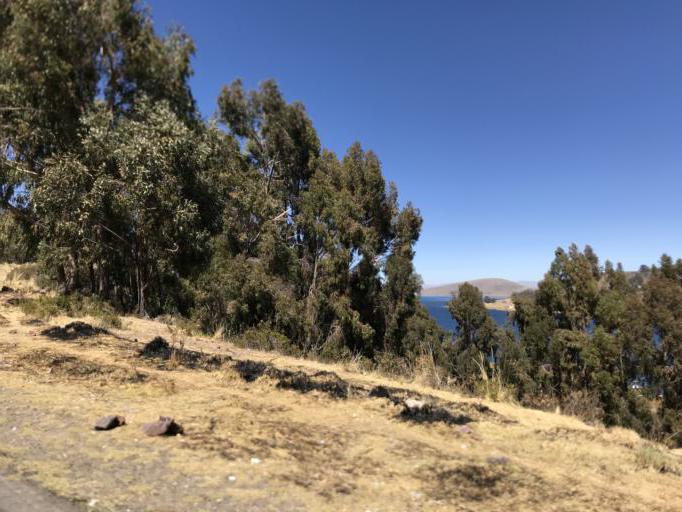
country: BO
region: La Paz
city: San Pablo
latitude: -16.2169
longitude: -68.8390
